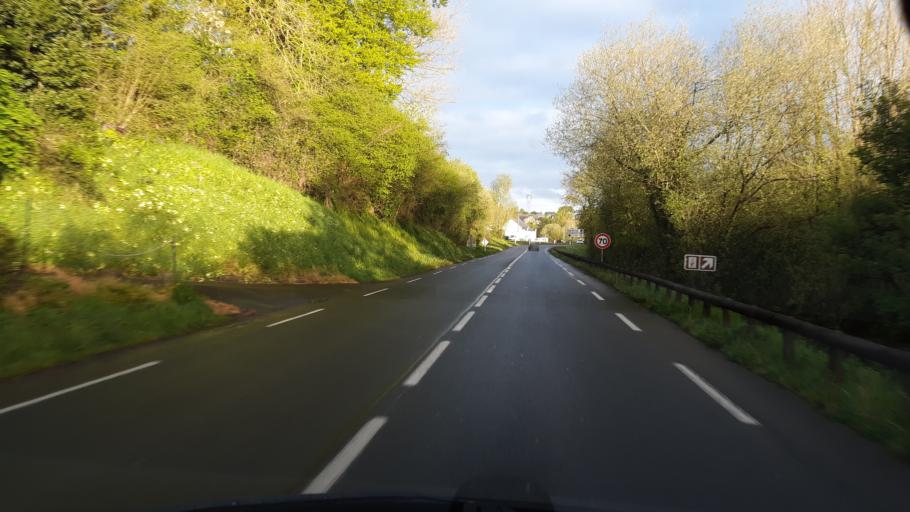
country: FR
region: Lower Normandy
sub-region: Departement de la Manche
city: Agneaux
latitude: 49.0885
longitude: -1.1165
